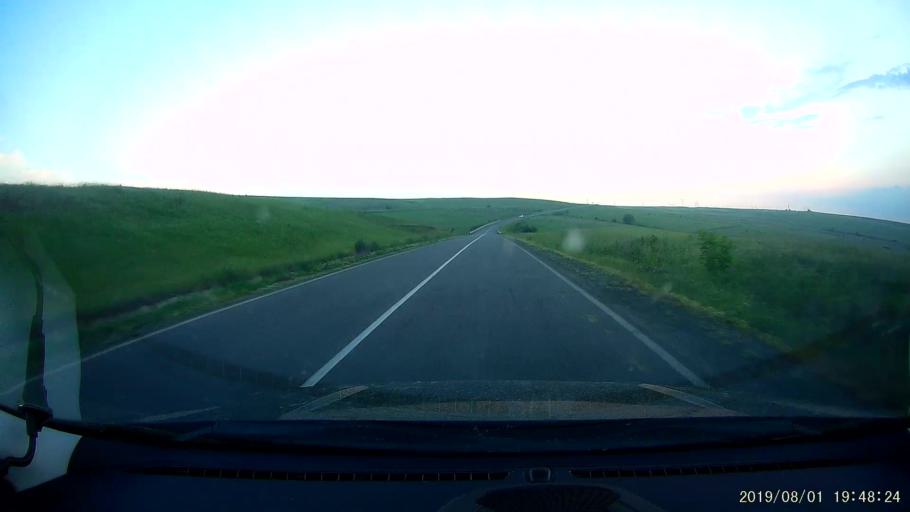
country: BG
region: Burgas
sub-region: Obshtina Karnobat
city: Karnobat
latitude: 42.6377
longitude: 26.9503
